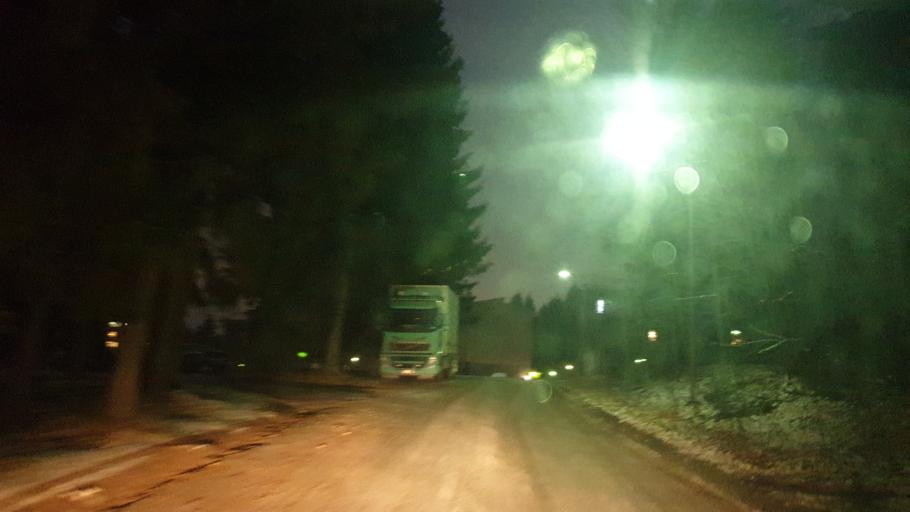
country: FI
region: Southern Savonia
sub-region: Savonlinna
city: Savonlinna
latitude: 61.8601
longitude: 28.9527
